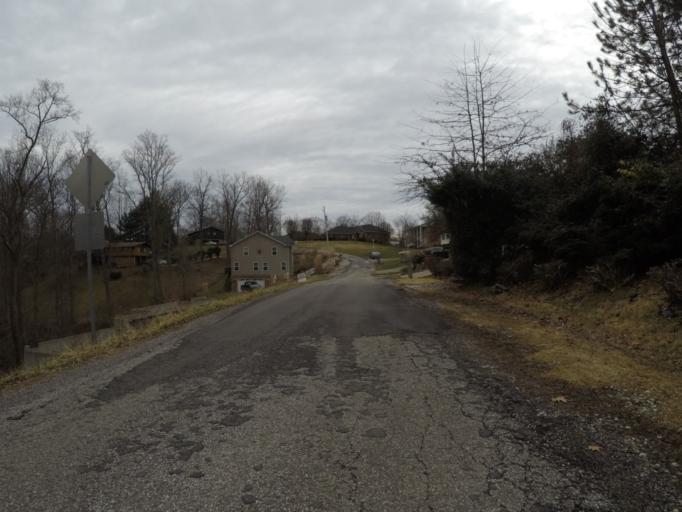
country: US
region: Ohio
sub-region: Lawrence County
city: Burlington
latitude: 38.3790
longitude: -82.5137
